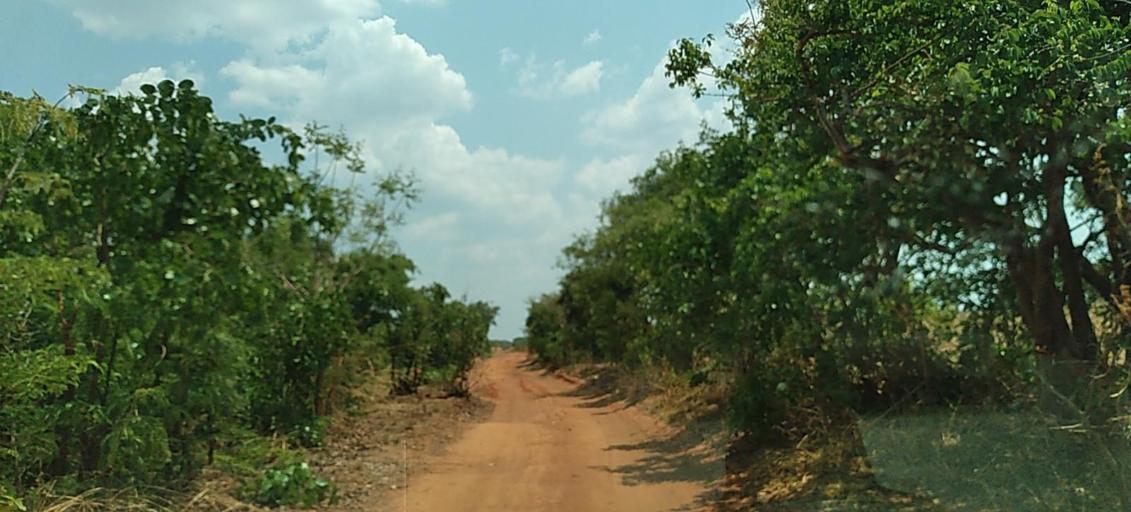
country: ZM
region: Copperbelt
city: Mpongwe
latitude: -13.6592
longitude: 28.0247
